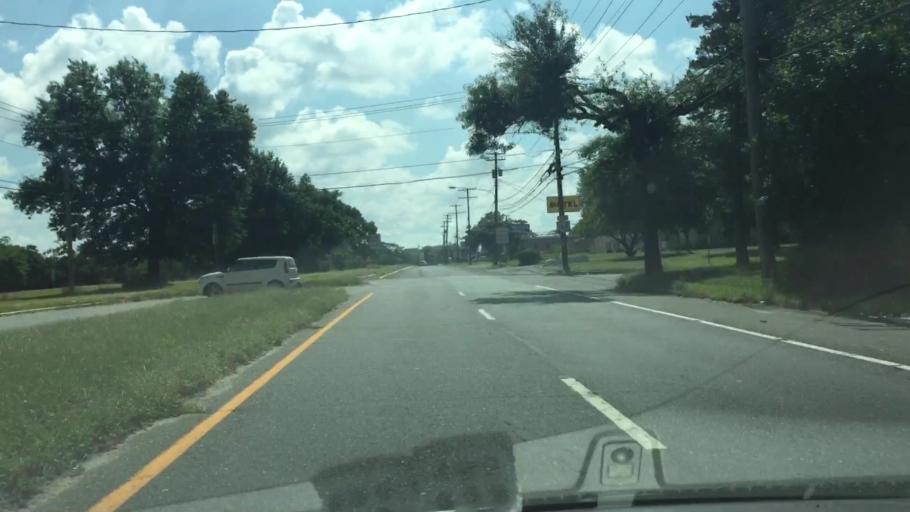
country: US
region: New Jersey
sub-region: Gloucester County
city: Turnersville
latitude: 39.7699
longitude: -75.0500
